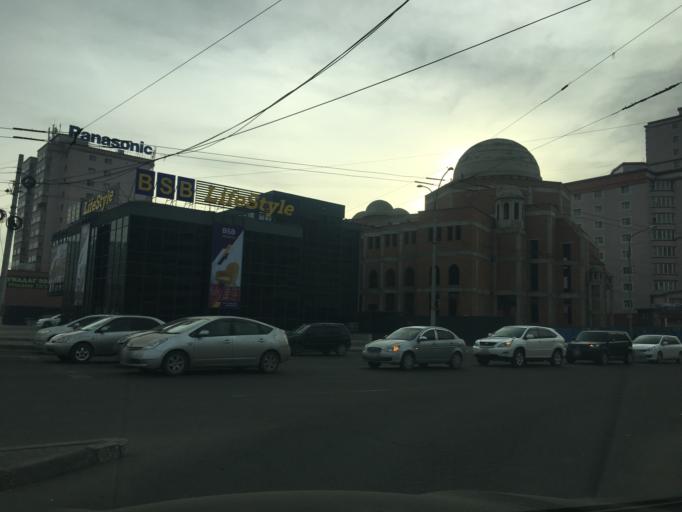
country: MN
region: Ulaanbaatar
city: Ulaanbaatar
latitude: 47.9145
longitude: 106.8837
